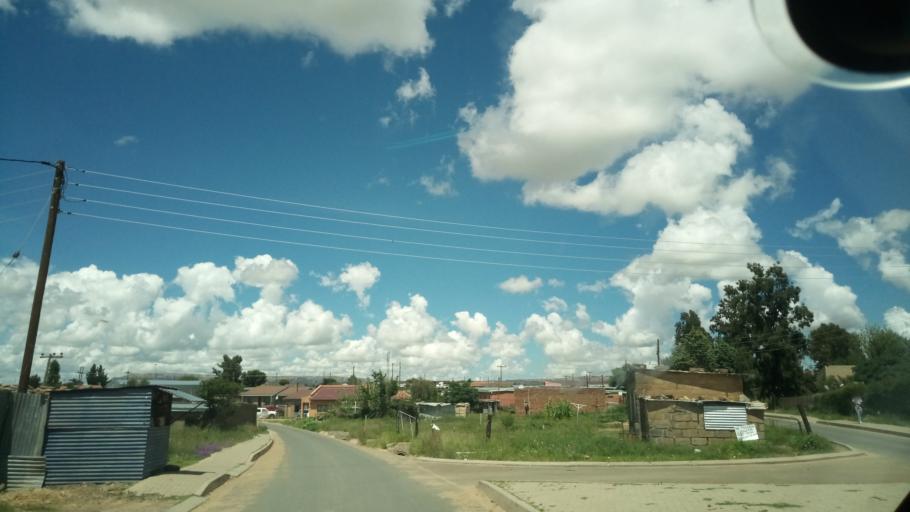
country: LS
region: Maseru
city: Maseru
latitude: -29.3678
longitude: 27.5400
